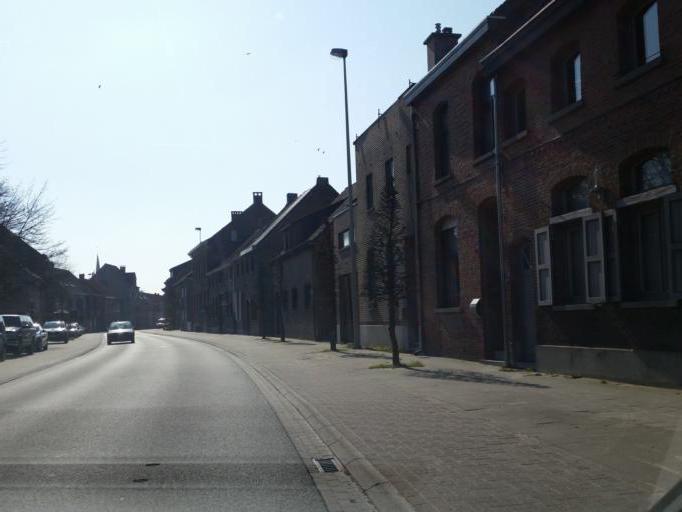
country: BE
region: Flanders
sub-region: Provincie Oost-Vlaanderen
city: Kruibeke
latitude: 51.1519
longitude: 4.2998
